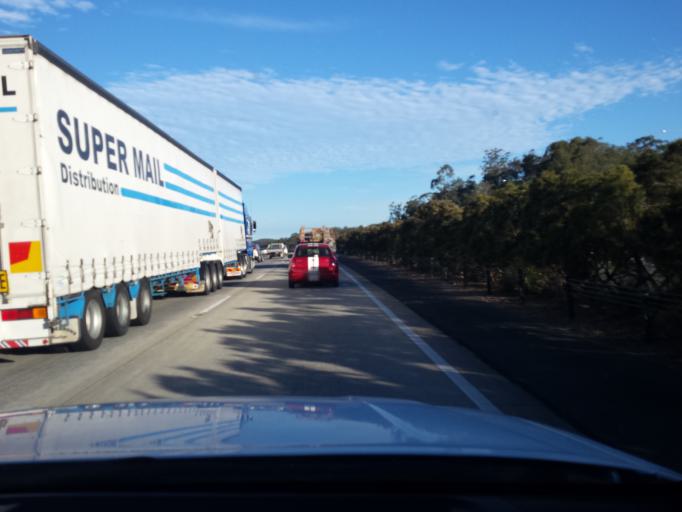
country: AU
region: Queensland
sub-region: Gold Coast
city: Ormeau Hills
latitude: -27.8065
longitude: 153.2661
